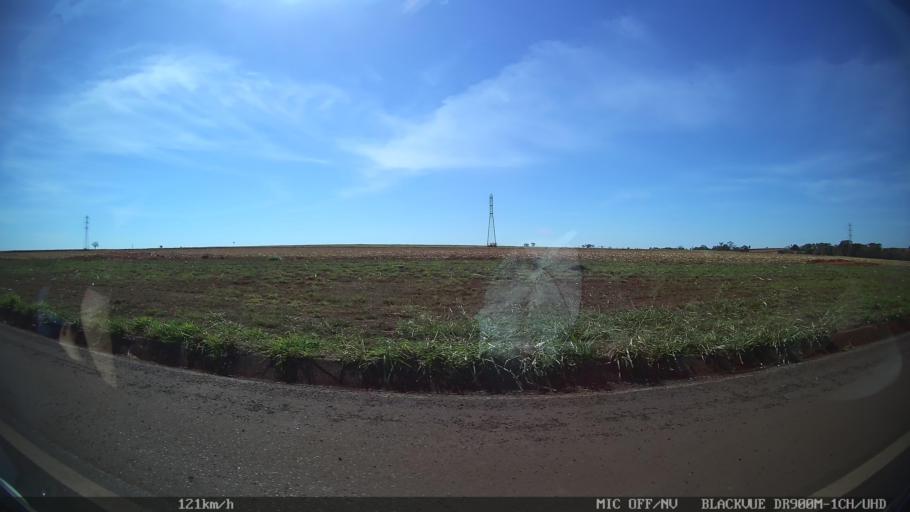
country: BR
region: Sao Paulo
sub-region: Ipua
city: Ipua
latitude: -20.4589
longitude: -48.1495
